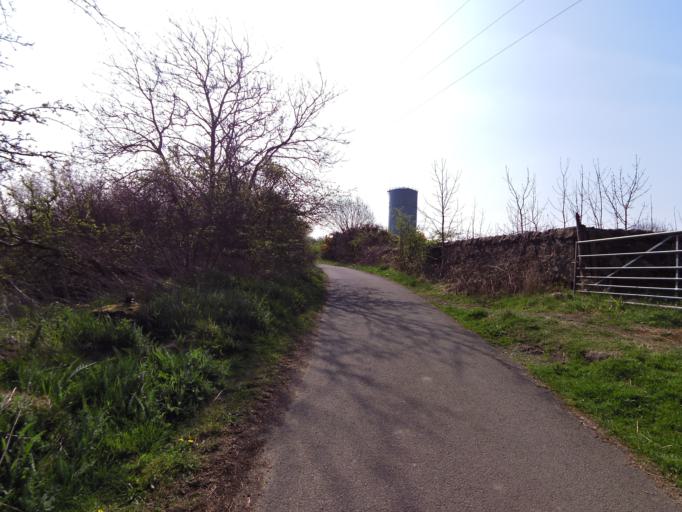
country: GB
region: Scotland
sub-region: Fife
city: Thornton
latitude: 56.1416
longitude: -3.1532
